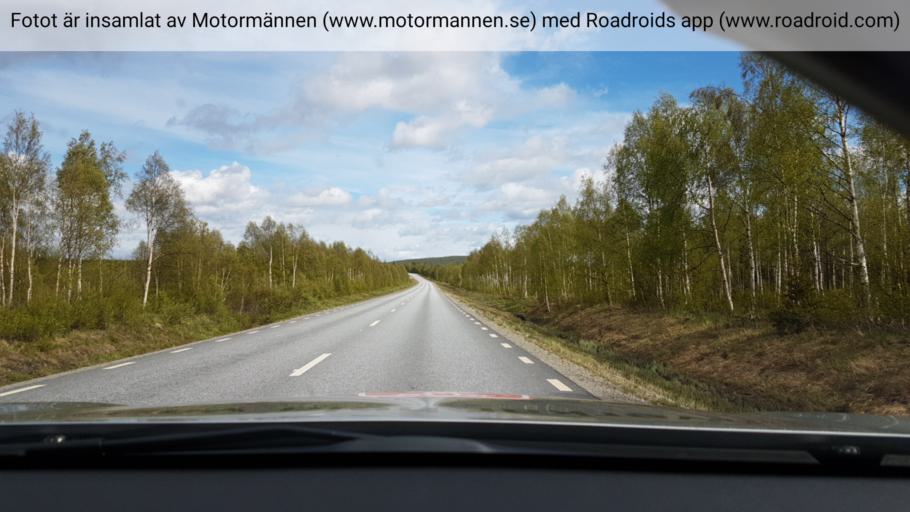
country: SE
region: Vaesterbotten
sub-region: Asele Kommun
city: Insjon
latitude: 64.1981
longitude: 17.5602
